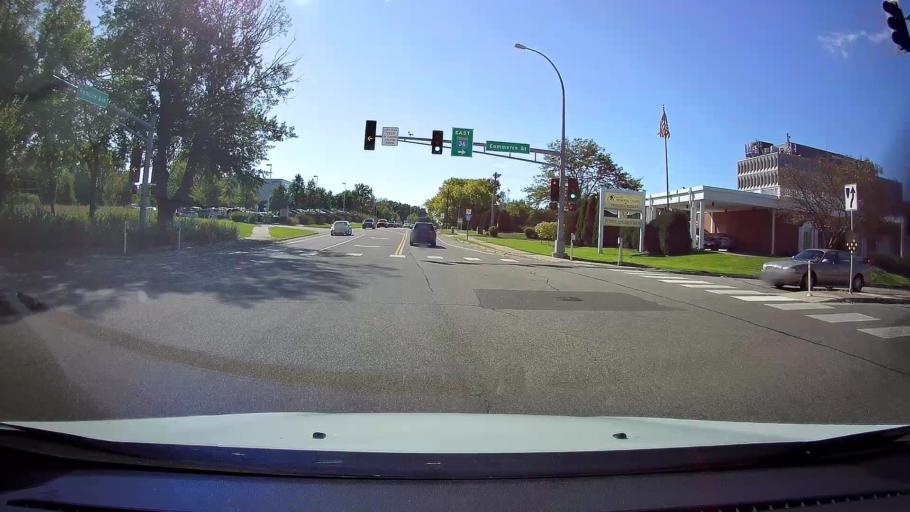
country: US
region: Minnesota
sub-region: Ramsey County
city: Roseville
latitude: 45.0090
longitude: -93.1567
